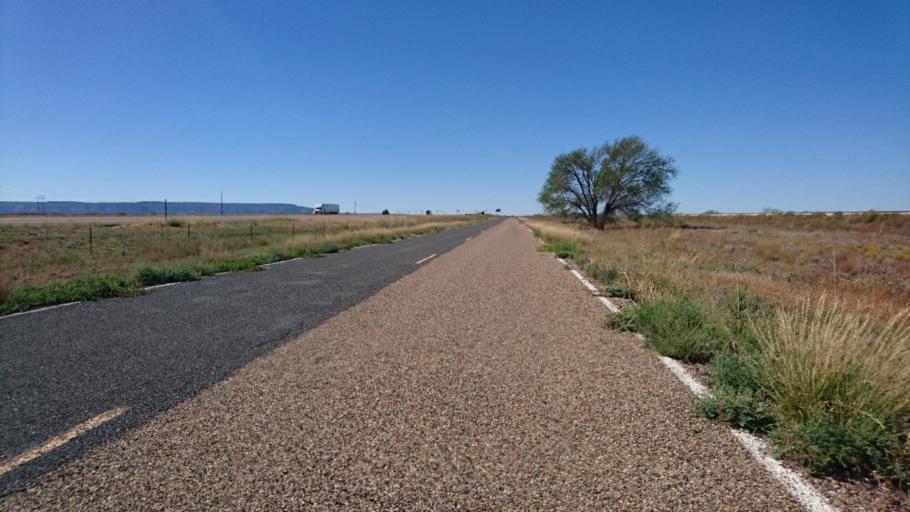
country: US
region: New Mexico
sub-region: Quay County
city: Tucumcari
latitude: 35.1020
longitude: -104.0430
